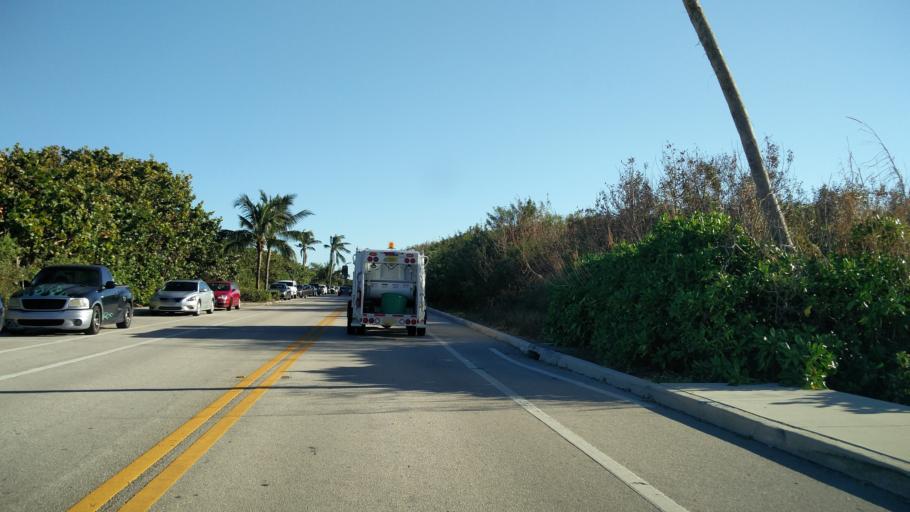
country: US
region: Florida
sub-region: Palm Beach County
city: Juno Beach
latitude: 26.9136
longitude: -80.0639
